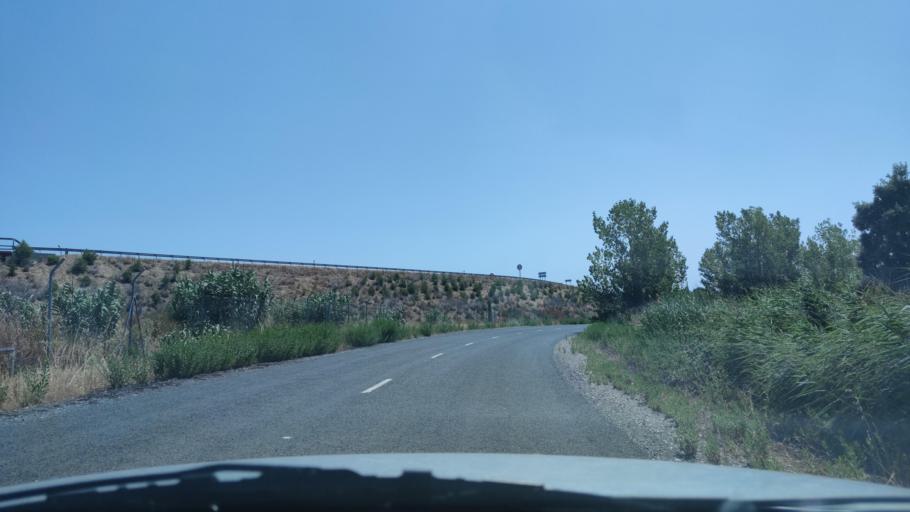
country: ES
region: Catalonia
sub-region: Provincia de Lleida
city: Torrefarrera
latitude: 41.6574
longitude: 0.5834
